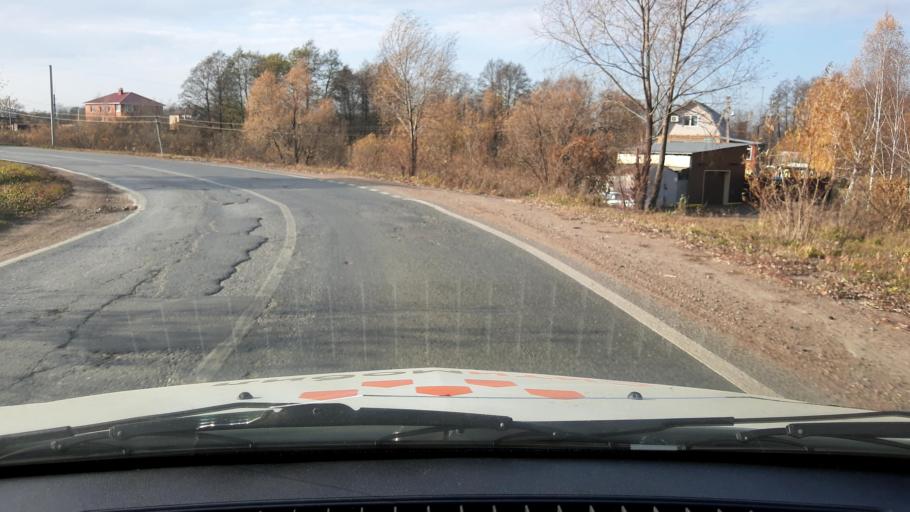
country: RU
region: Bashkortostan
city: Kabakovo
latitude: 54.7468
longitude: 56.2114
